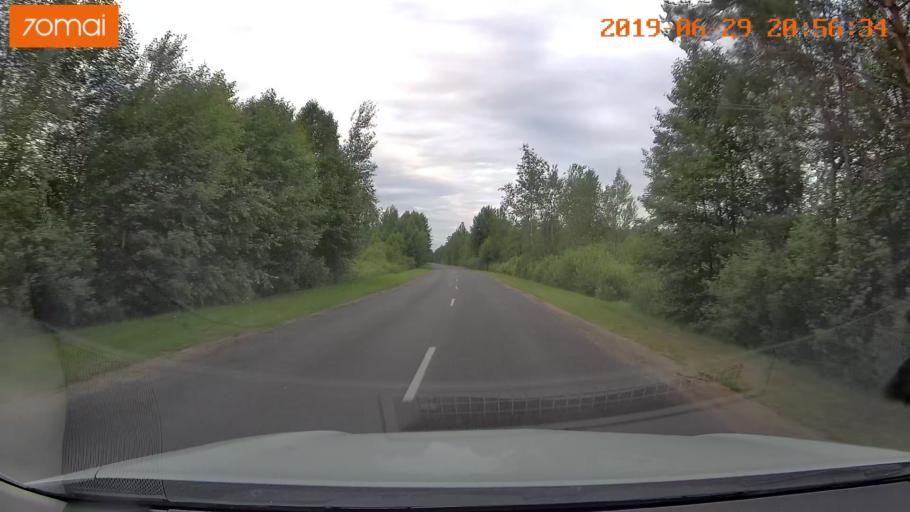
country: BY
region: Brest
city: Hantsavichy
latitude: 52.7071
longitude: 26.3683
